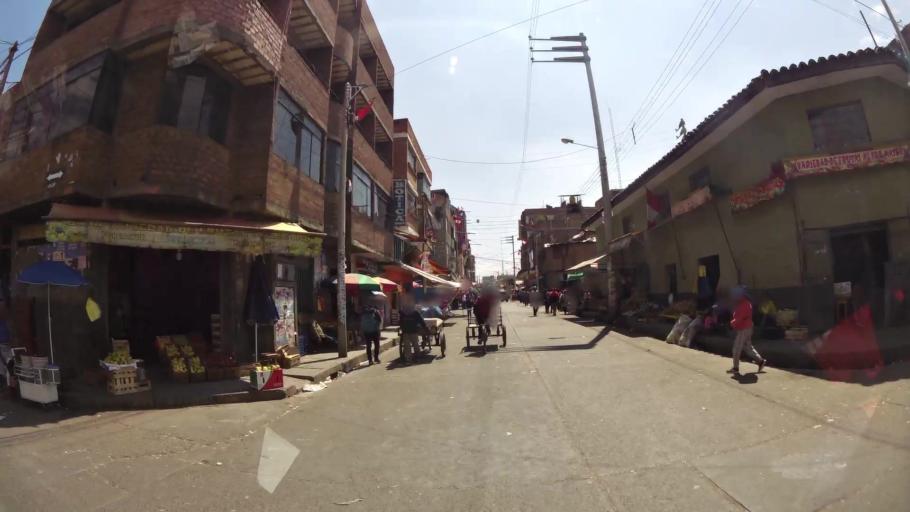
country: PE
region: Junin
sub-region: Provincia de Huancayo
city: Huancayo
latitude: -12.0695
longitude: -75.2020
